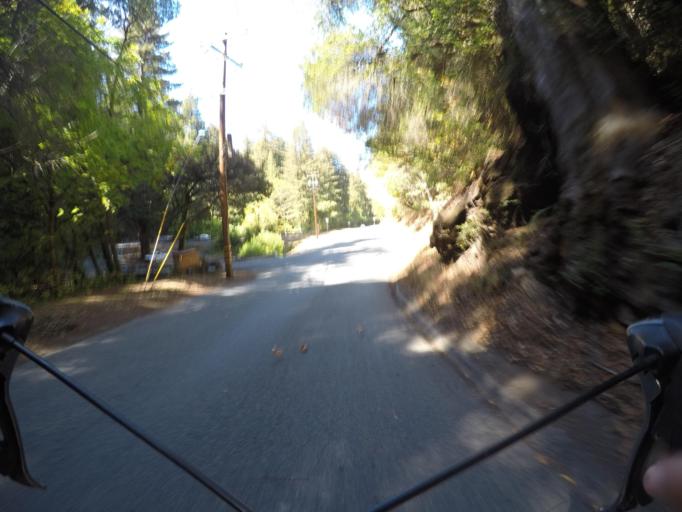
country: US
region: California
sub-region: San Mateo County
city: Portola Valley
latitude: 37.2994
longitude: -122.2640
